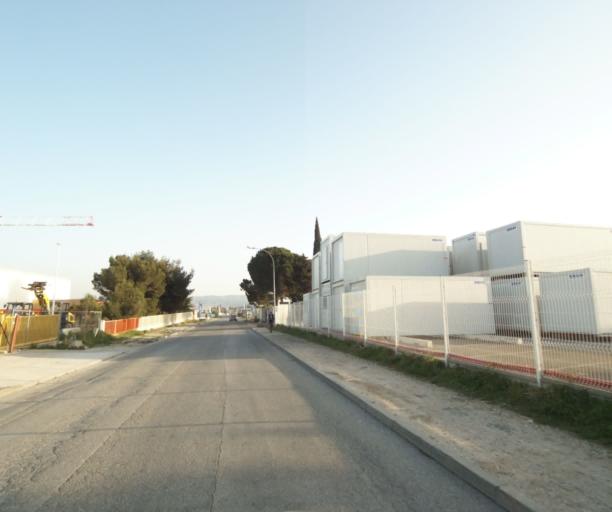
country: FR
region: Provence-Alpes-Cote d'Azur
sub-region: Departement des Bouches-du-Rhone
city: Saint-Victoret
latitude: 43.4362
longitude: 5.2508
